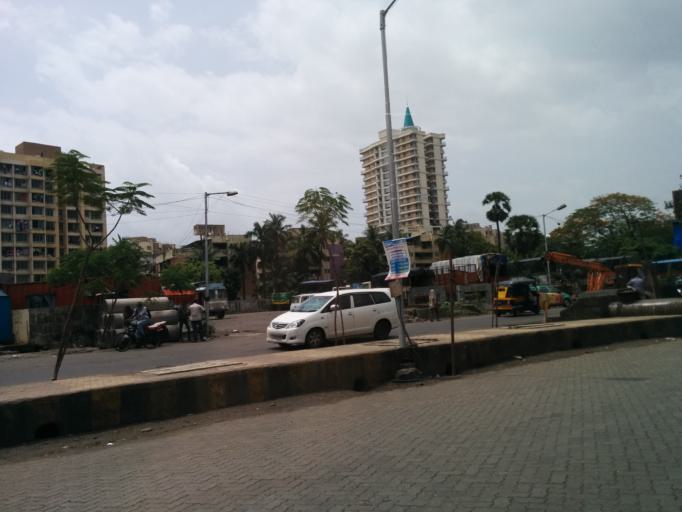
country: IN
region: Maharashtra
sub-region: Thane
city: Thane
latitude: 19.2119
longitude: 72.9763
